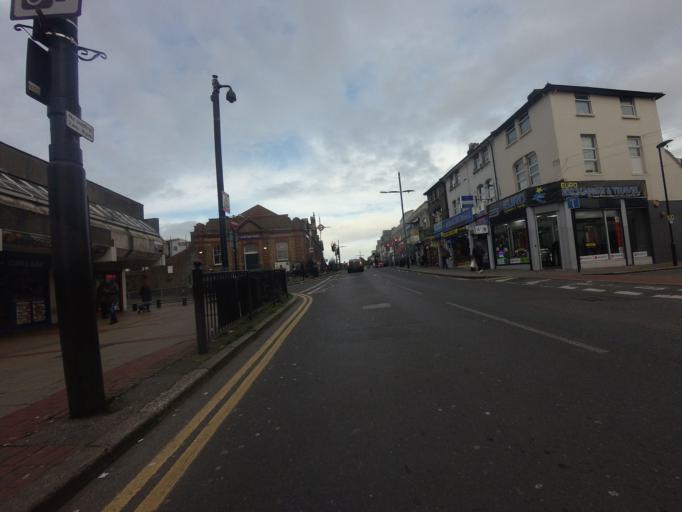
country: GB
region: England
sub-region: Greater London
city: East Ham
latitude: 51.5350
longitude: 0.0355
